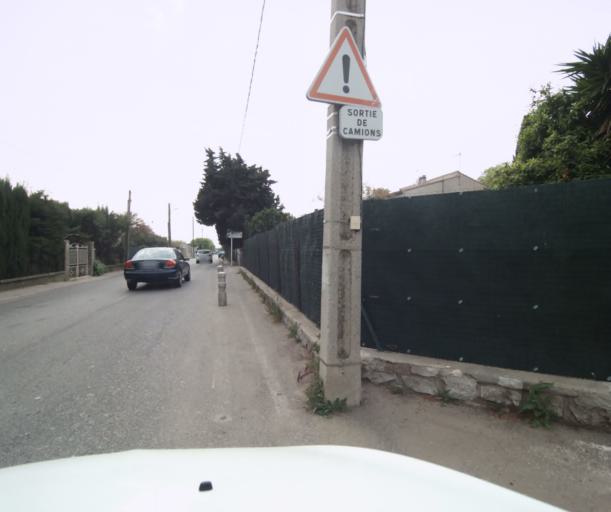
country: FR
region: Provence-Alpes-Cote d'Azur
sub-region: Departement du Var
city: La Valette-du-Var
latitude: 43.1293
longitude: 5.9852
